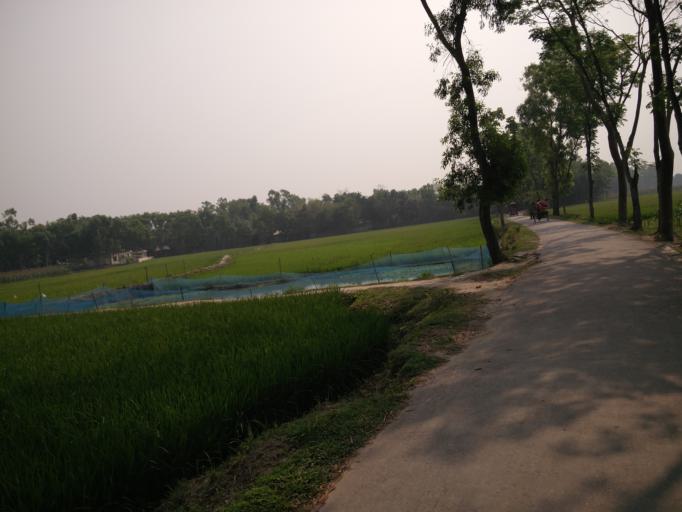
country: BD
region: Dhaka
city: Muktagacha
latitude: 24.9152
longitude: 90.2216
